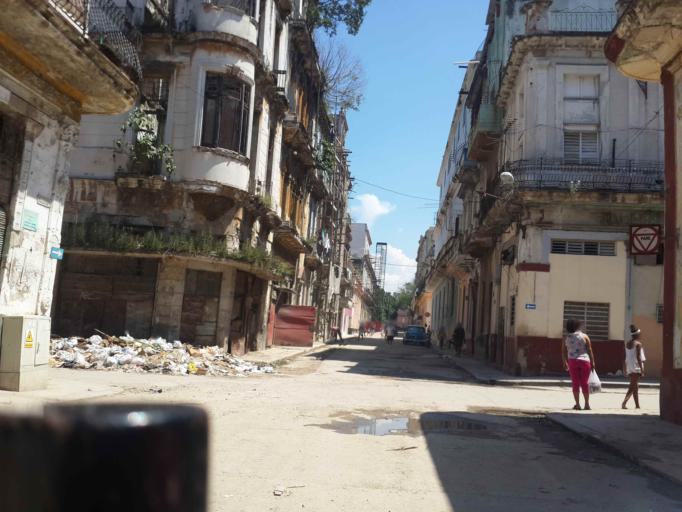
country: CU
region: La Habana
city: Centro Habana
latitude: 23.1398
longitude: -82.3609
